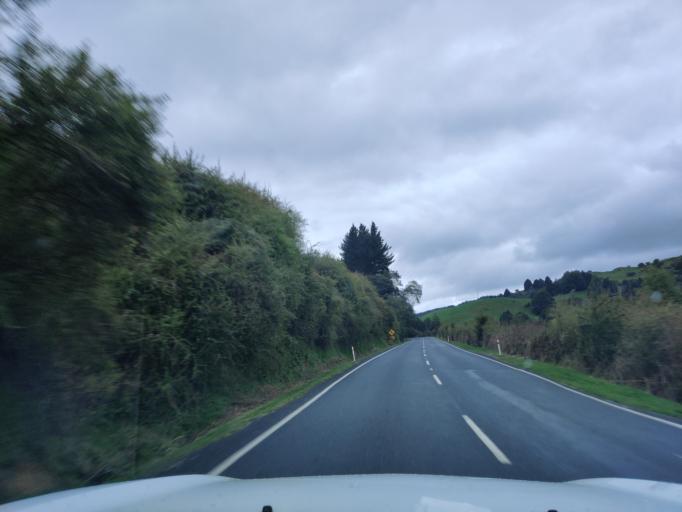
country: NZ
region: Waikato
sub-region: Otorohanga District
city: Otorohanga
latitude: -38.5906
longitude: 175.2175
